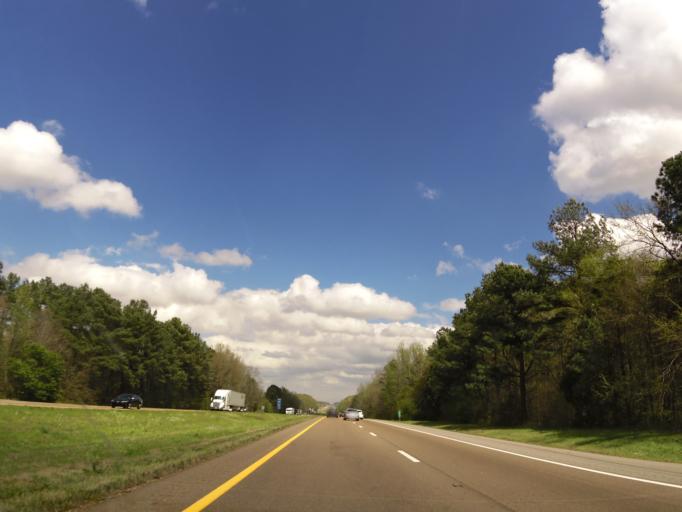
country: US
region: Tennessee
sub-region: Shelby County
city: Lakeland
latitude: 35.2447
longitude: -89.6986
